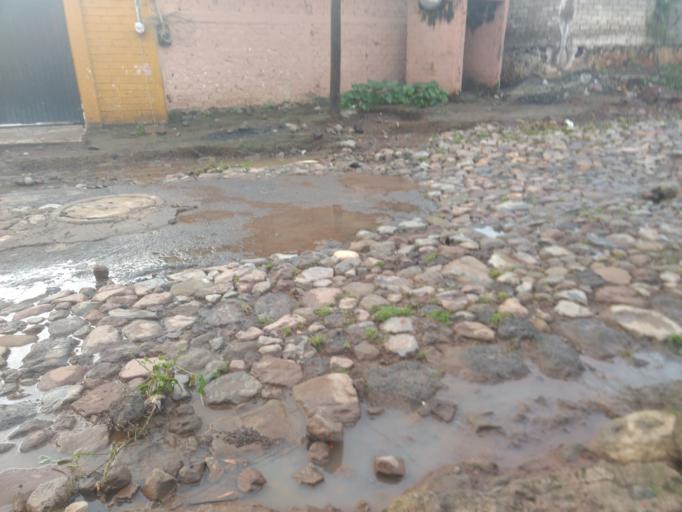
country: MX
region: Nayarit
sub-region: Tepic
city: La Corregidora
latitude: 21.4615
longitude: -104.8048
